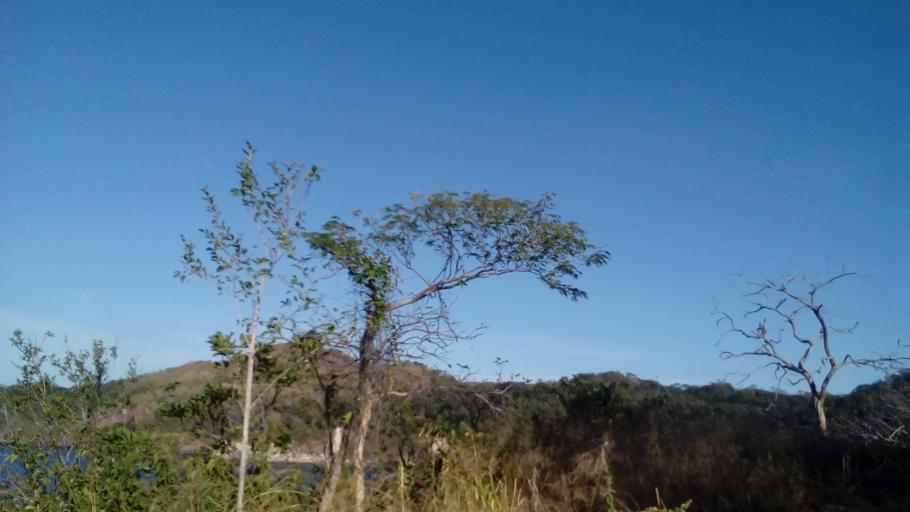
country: CR
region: Guanacaste
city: Sardinal
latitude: 10.3986
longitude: -85.8344
